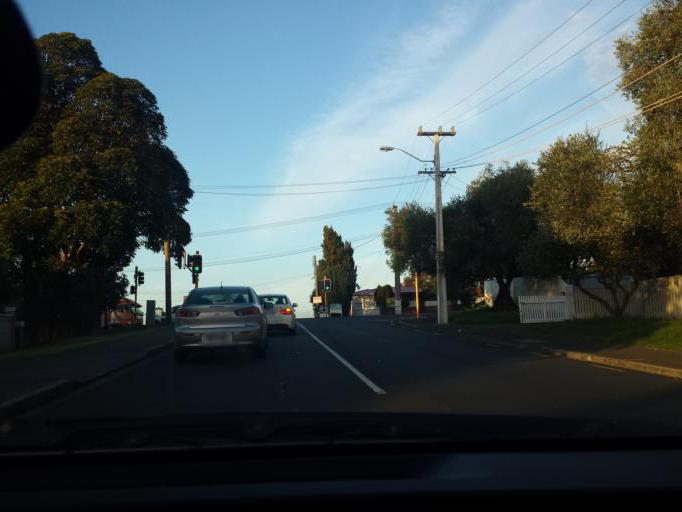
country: NZ
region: Auckland
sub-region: Auckland
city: Tamaki
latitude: -36.9063
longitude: 174.8349
